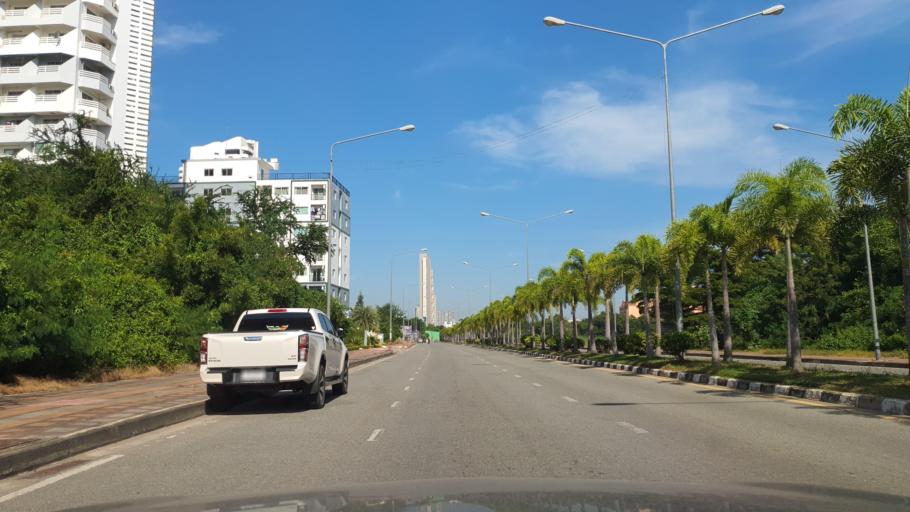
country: TH
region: Chon Buri
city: Phatthaya
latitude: 12.8735
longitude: 100.8924
